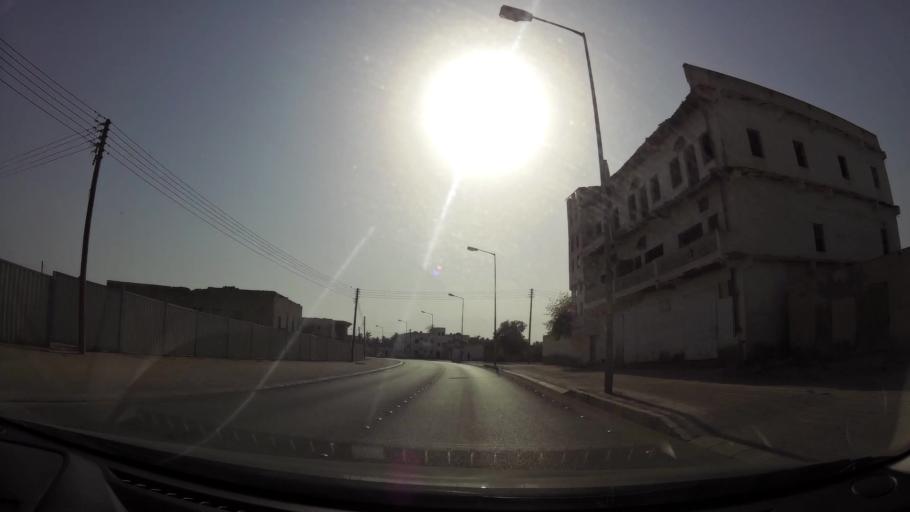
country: OM
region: Zufar
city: Salalah
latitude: 17.0035
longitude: 54.1082
